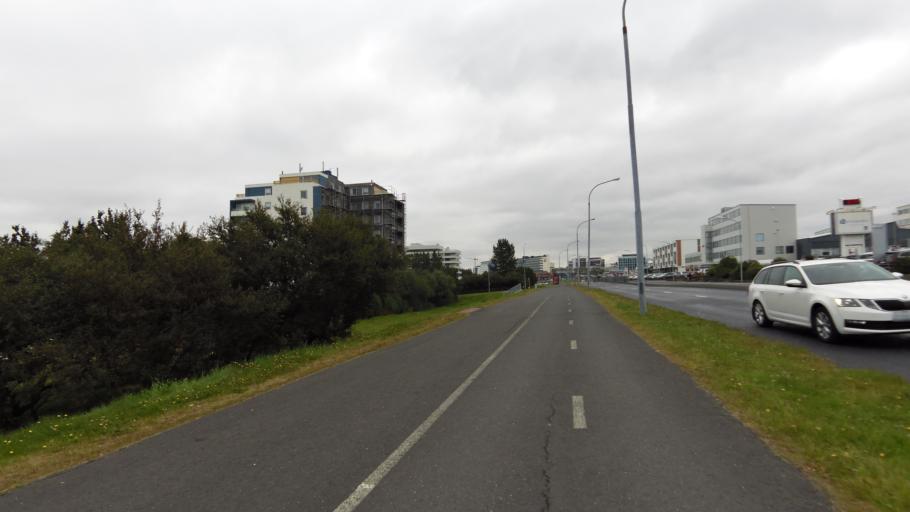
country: IS
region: Capital Region
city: Reykjavik
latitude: 64.1417
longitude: -21.9007
